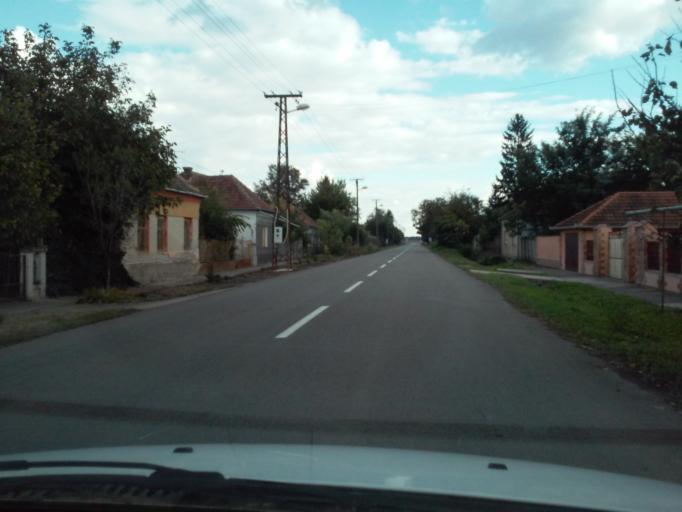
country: RS
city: Sajan
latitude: 45.8383
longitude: 20.2829
